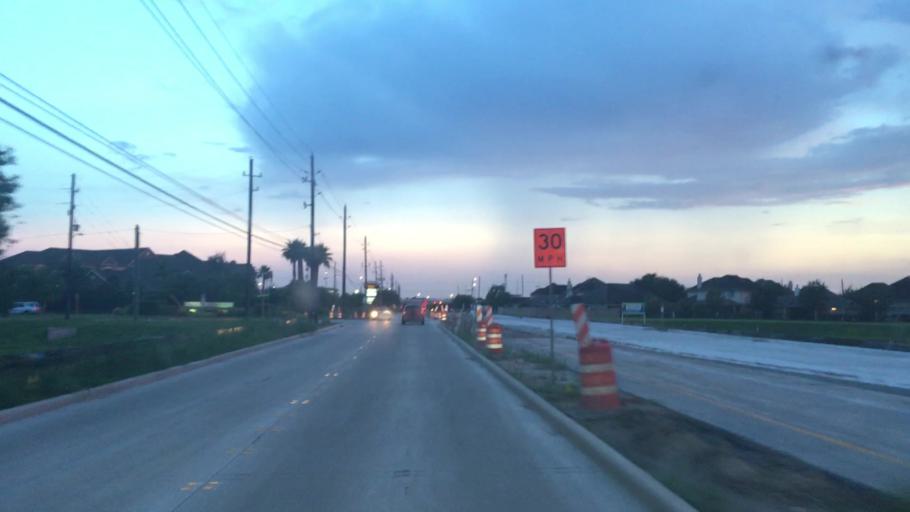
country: US
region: Texas
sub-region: Harris County
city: Humble
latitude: 29.9403
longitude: -95.2496
